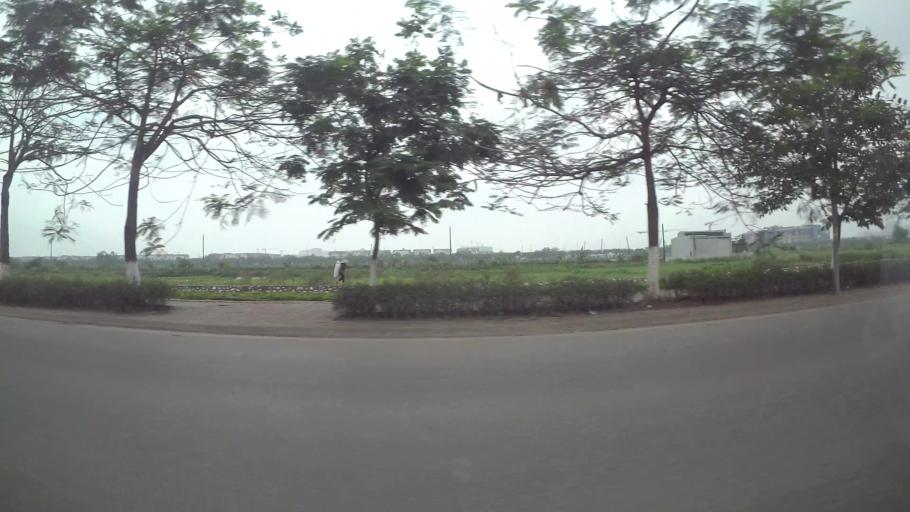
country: VN
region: Ha Noi
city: Trau Quy
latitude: 21.0492
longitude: 105.9224
